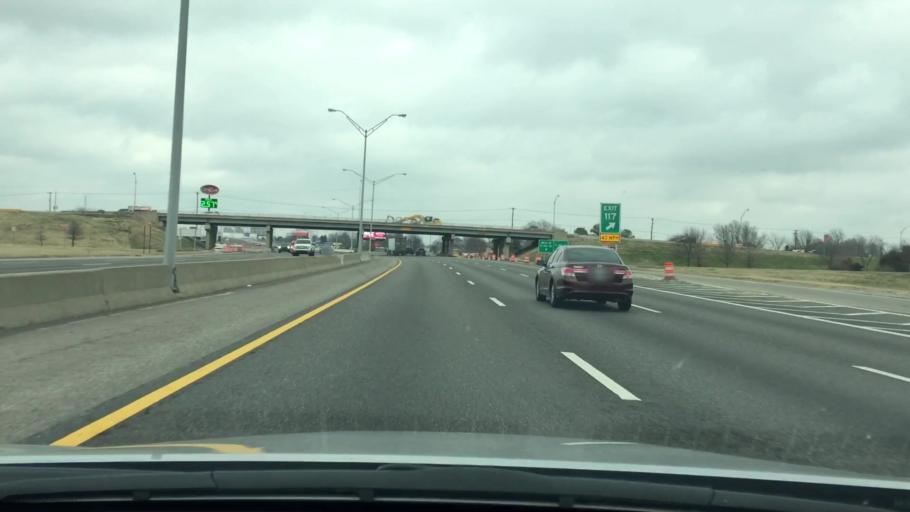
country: US
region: Oklahoma
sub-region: Cleveland County
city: Moore
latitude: 35.3321
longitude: -97.4900
